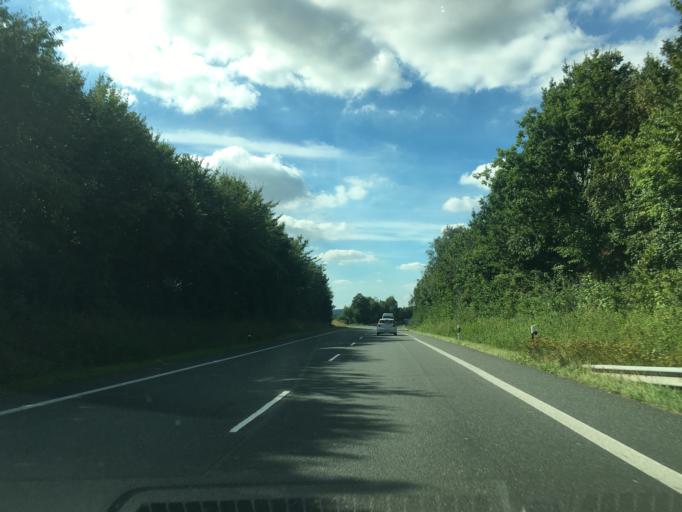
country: DE
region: North Rhine-Westphalia
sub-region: Regierungsbezirk Detmold
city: Dorentrup
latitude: 51.9791
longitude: 9.0137
